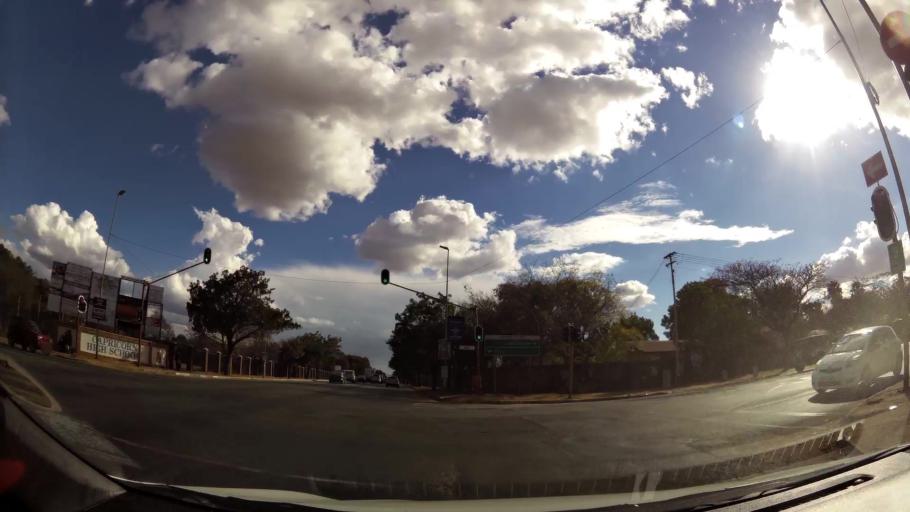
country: ZA
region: Limpopo
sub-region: Capricorn District Municipality
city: Polokwane
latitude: -23.9072
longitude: 29.4737
